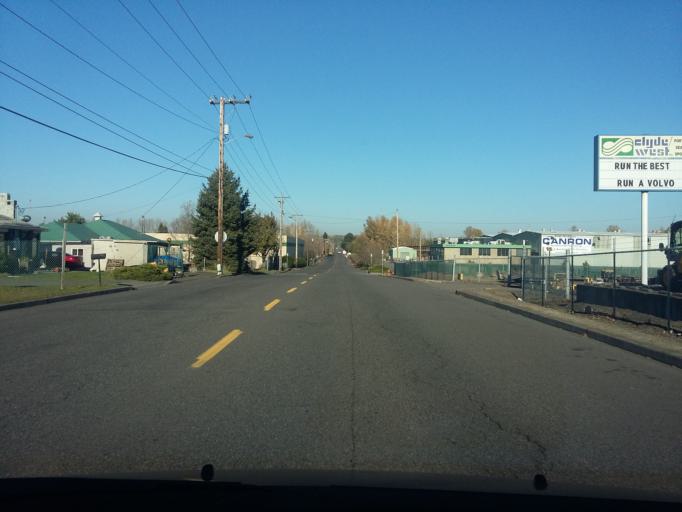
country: US
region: Oregon
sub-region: Multnomah County
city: Lents
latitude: 45.5552
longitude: -122.5211
